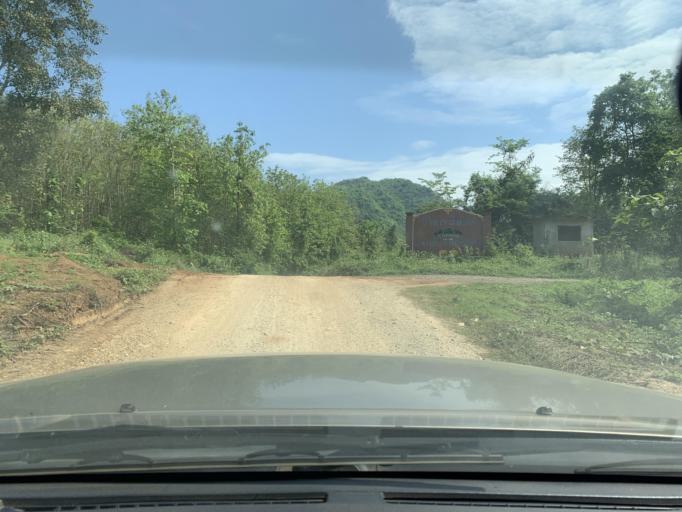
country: LA
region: Louangphabang
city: Louangphabang
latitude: 19.8872
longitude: 102.1972
